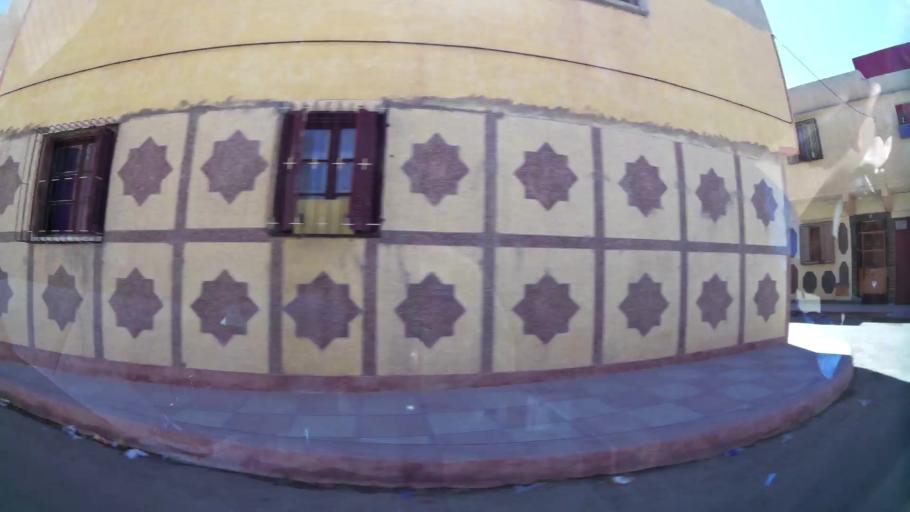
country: MA
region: Oriental
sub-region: Oujda-Angad
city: Oujda
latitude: 34.6665
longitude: -1.9351
